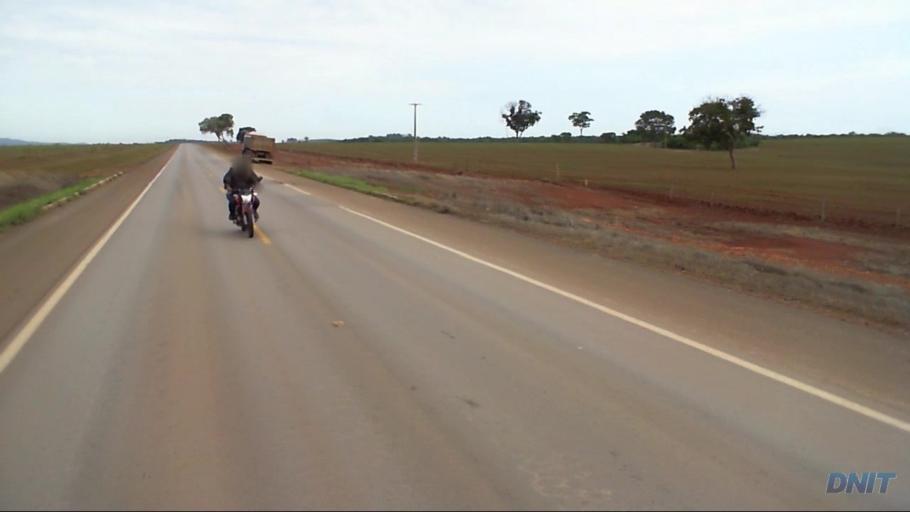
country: BR
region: Goias
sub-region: Uruacu
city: Uruacu
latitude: -14.7023
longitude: -49.1169
